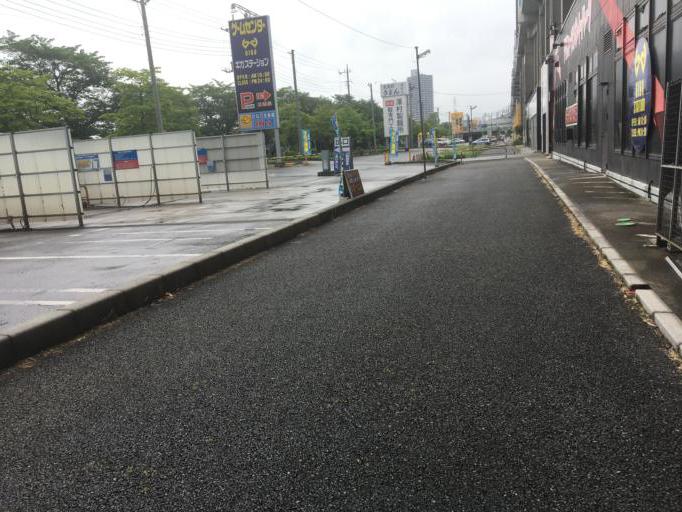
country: JP
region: Saitama
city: Shimotoda
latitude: 35.8344
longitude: 139.6534
